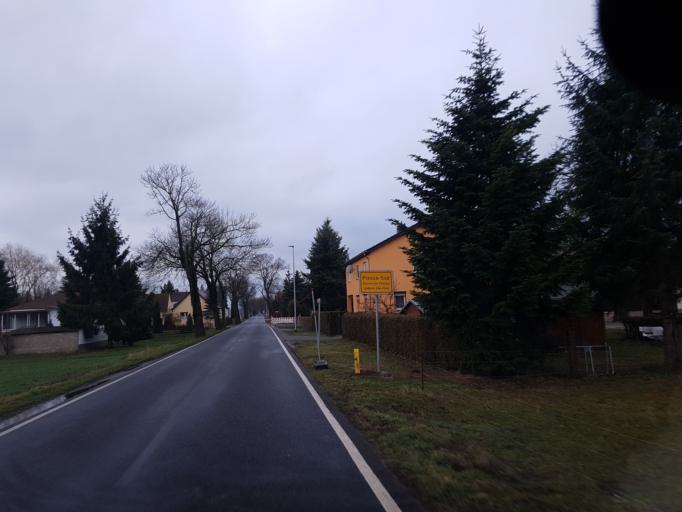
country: DE
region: Brandenburg
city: Plessa
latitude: 51.4332
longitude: 13.6249
